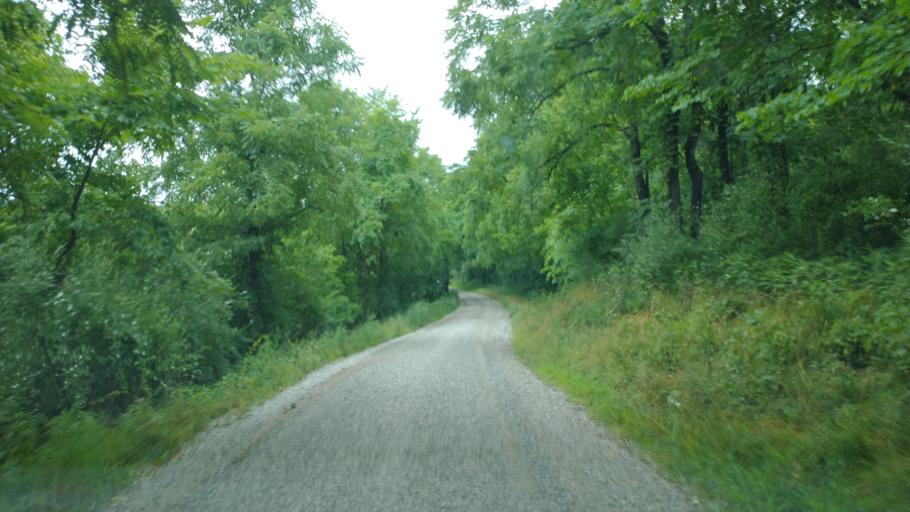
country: US
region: Ohio
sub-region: Meigs County
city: Middleport
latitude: 38.9284
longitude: -82.0624
